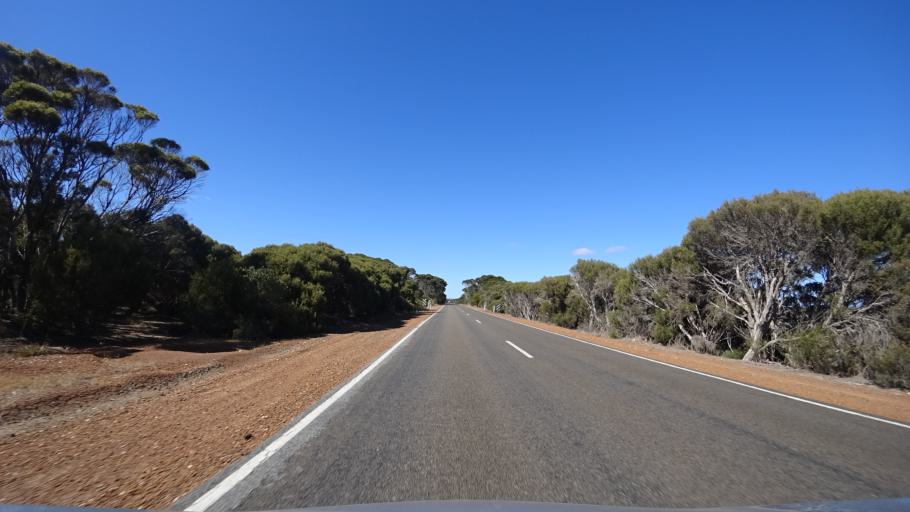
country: AU
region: South Australia
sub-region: Kangaroo Island
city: Kingscote
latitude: -35.7082
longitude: 137.5654
